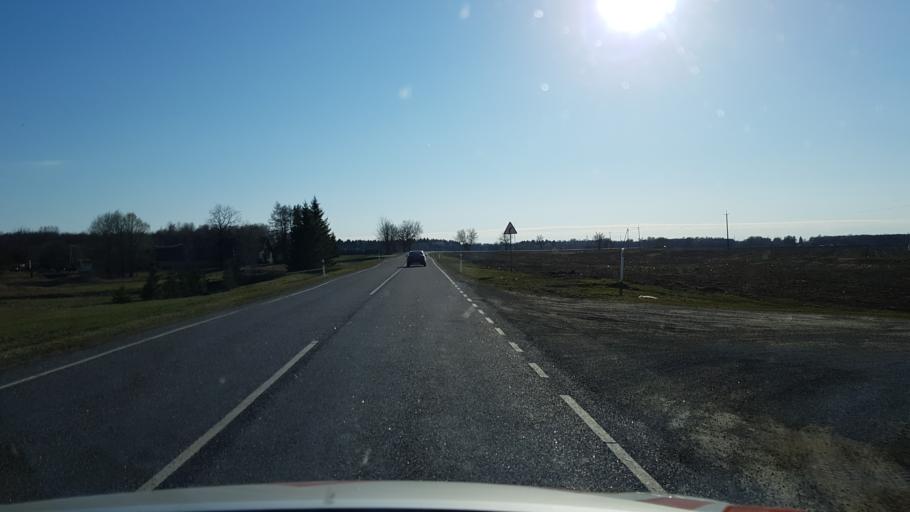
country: EE
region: Ida-Virumaa
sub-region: Kohtla-Jaerve linn
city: Kohtla-Jarve
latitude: 59.3369
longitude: 27.3344
